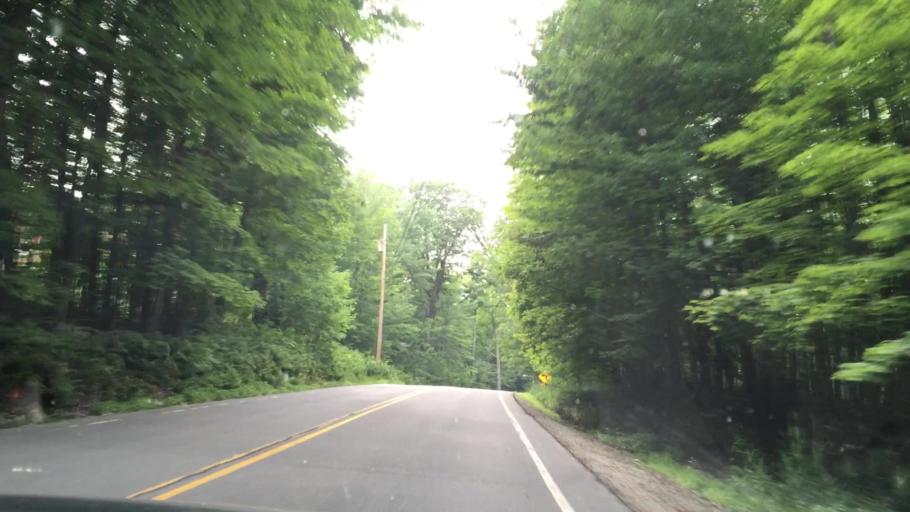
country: US
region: New Hampshire
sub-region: Belknap County
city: Meredith
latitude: 43.7035
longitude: -71.5078
